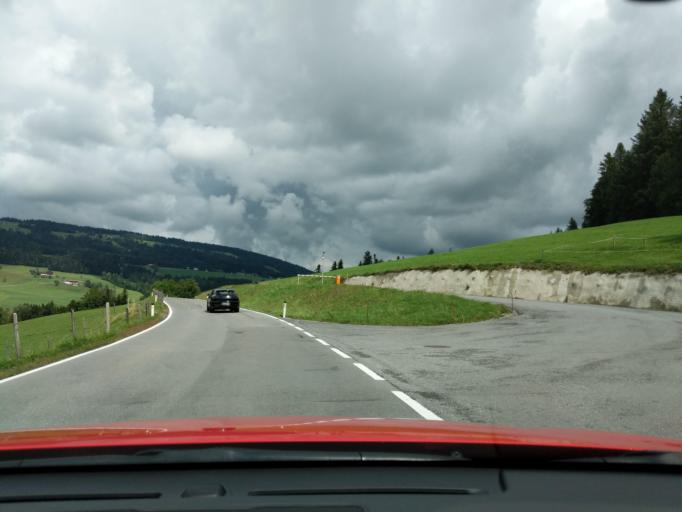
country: AT
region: Vorarlberg
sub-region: Politischer Bezirk Bregenz
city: Riefensberg
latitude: 47.5023
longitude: 9.9463
